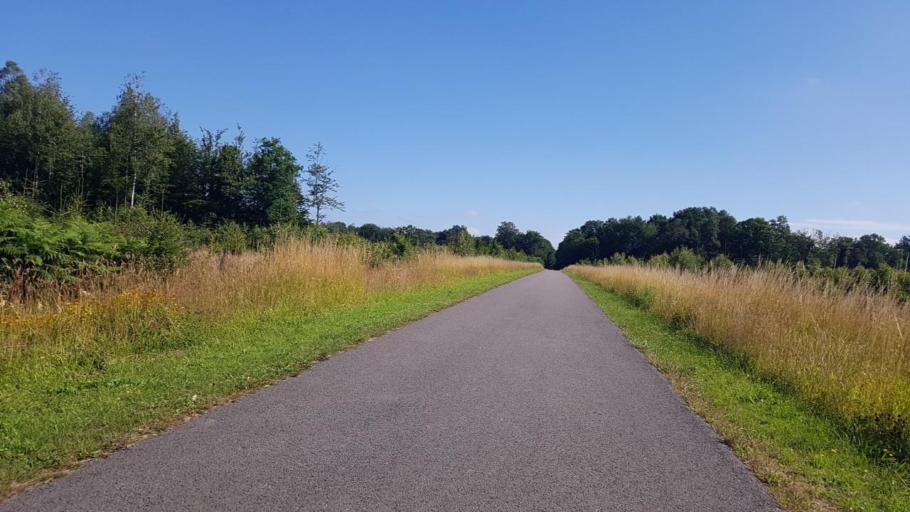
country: FR
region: Nord-Pas-de-Calais
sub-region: Departement du Nord
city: Anor
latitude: 49.9625
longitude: 4.1122
